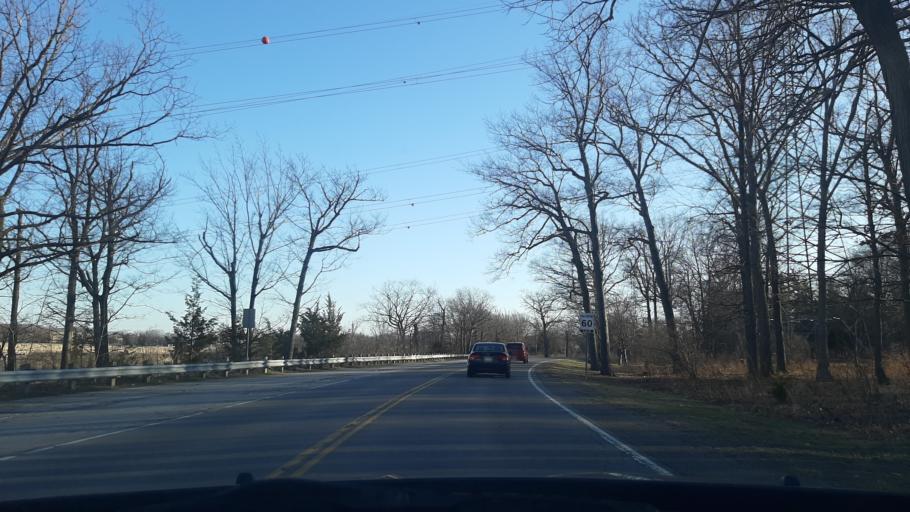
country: US
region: New York
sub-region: Niagara County
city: Lewiston
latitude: 43.1447
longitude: -79.0450
